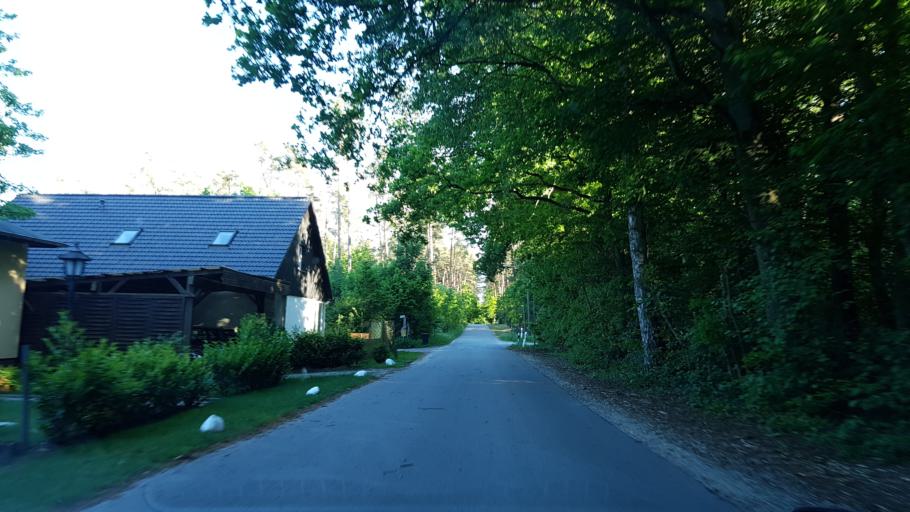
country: DE
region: Lower Saxony
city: Stelle
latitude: 53.3566
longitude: 10.1045
